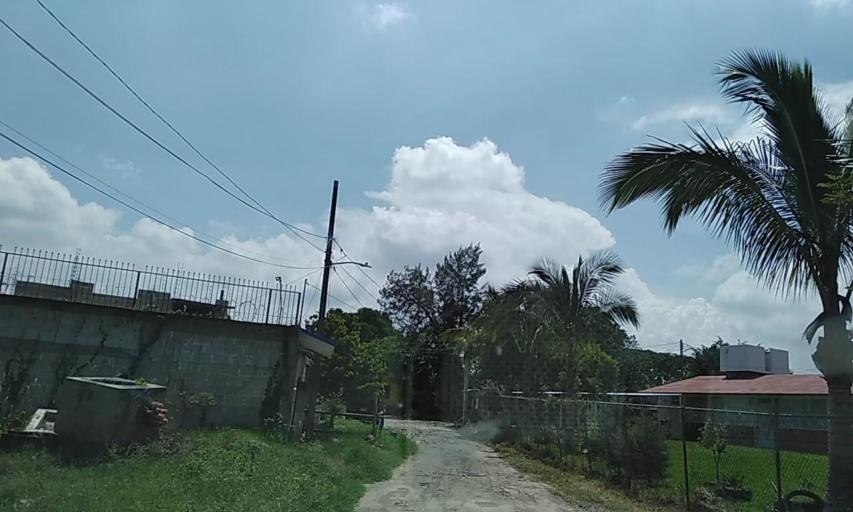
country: MX
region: Veracruz
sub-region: Emiliano Zapata
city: Dos Rios
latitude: 19.4435
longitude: -96.7800
